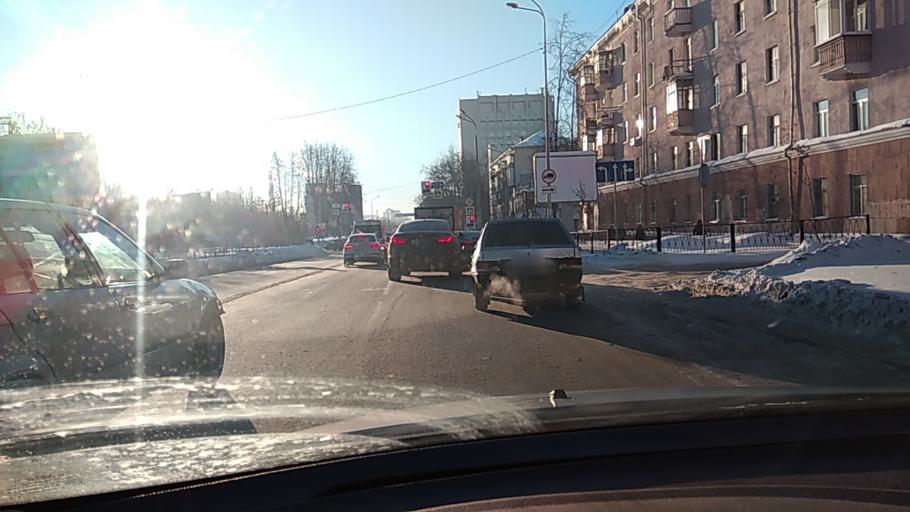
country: RU
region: Sverdlovsk
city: Yekaterinburg
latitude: 56.8449
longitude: 60.6307
